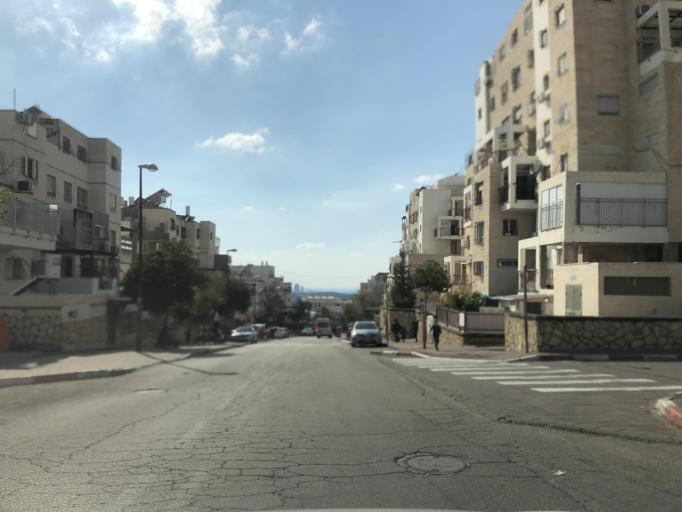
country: IL
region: Jerusalem
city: Modiin Ilit
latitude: 31.9402
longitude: 35.0400
